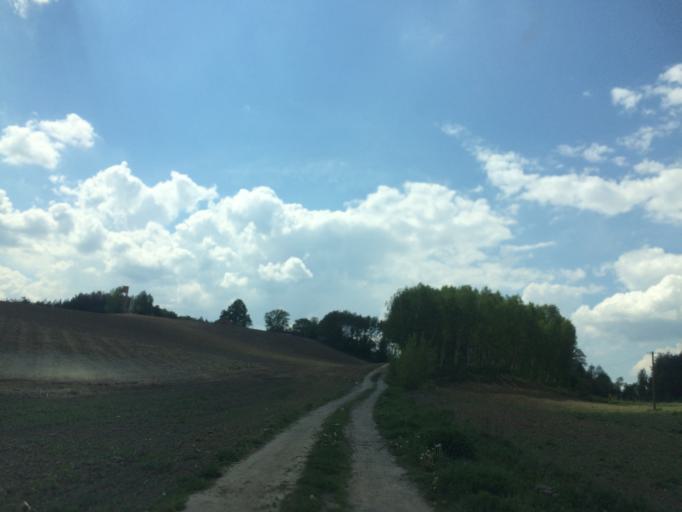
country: PL
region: Warmian-Masurian Voivodeship
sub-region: Powiat nowomiejski
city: Nowe Miasto Lubawskie
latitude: 53.4493
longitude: 19.5837
